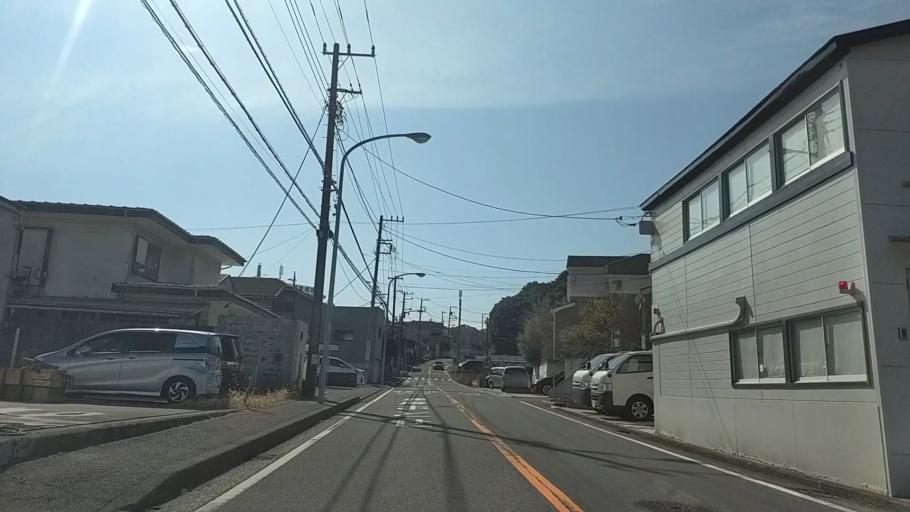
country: JP
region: Kanagawa
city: Kamakura
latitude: 35.3980
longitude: 139.5562
